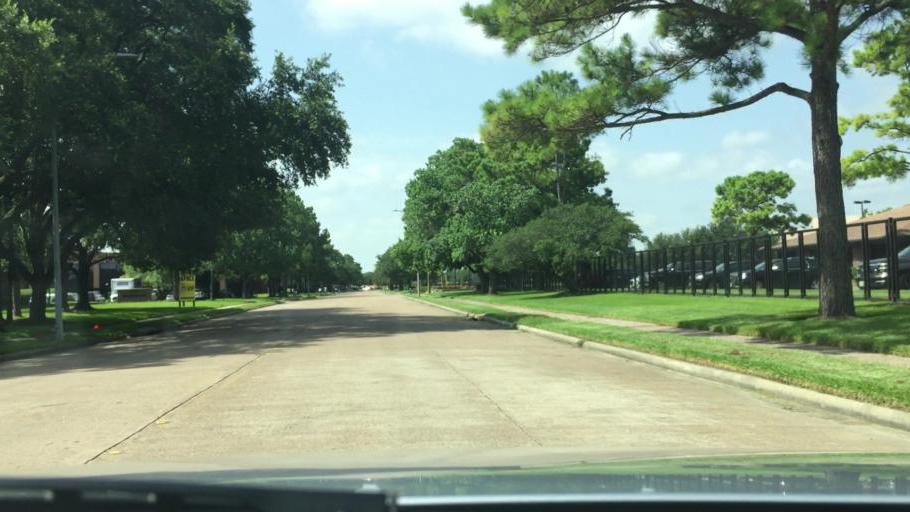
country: US
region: Texas
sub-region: Harris County
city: Hudson
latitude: 29.8485
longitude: -95.4949
